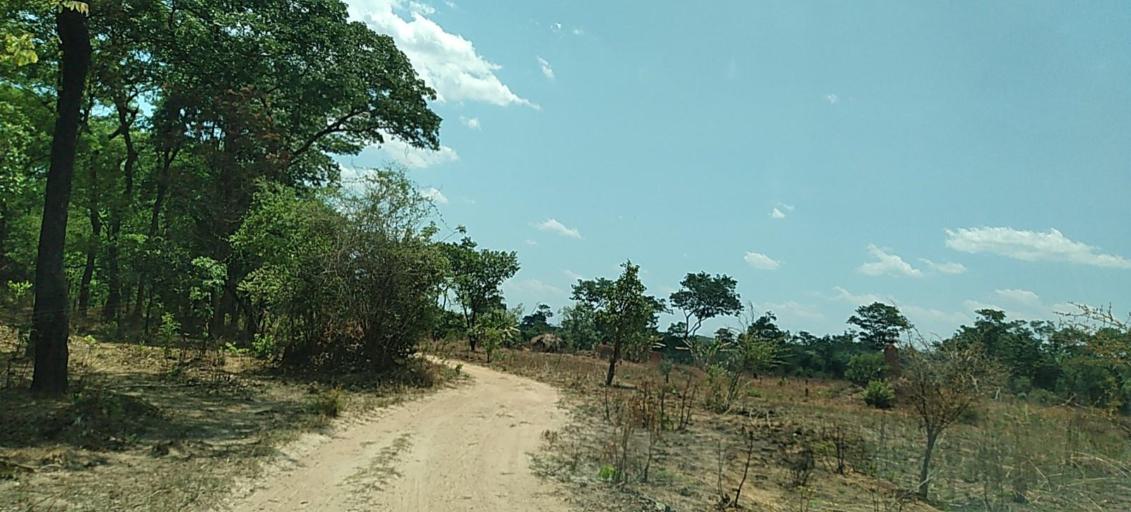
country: ZM
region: Central
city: Kapiri Mposhi
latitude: -13.6315
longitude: 28.7653
